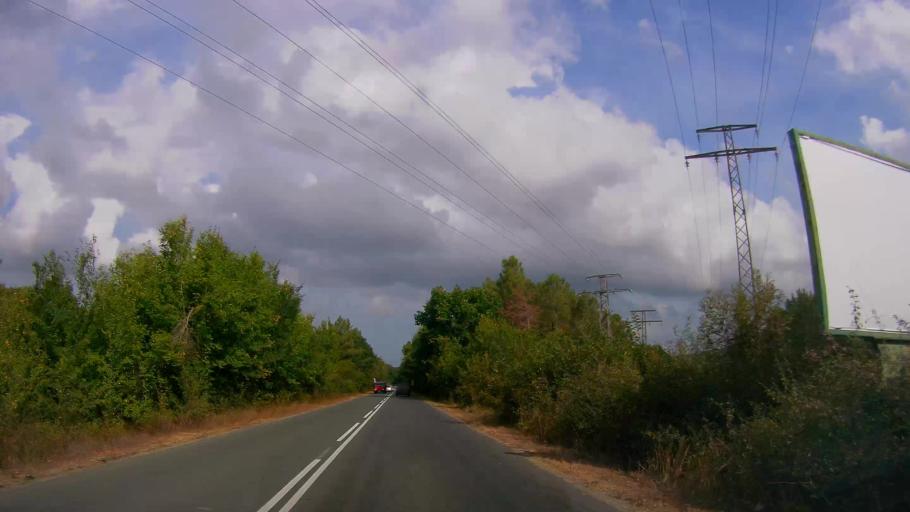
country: BG
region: Burgas
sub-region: Obshtina Primorsko
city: Primorsko
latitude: 42.2729
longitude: 27.7416
